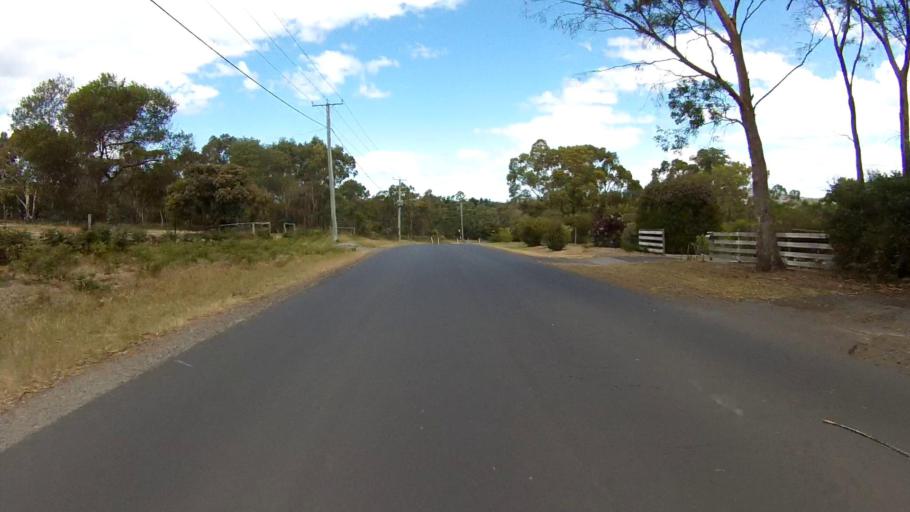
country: AU
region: Tasmania
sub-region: Clarence
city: Acton Park
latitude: -42.8760
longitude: 147.4900
